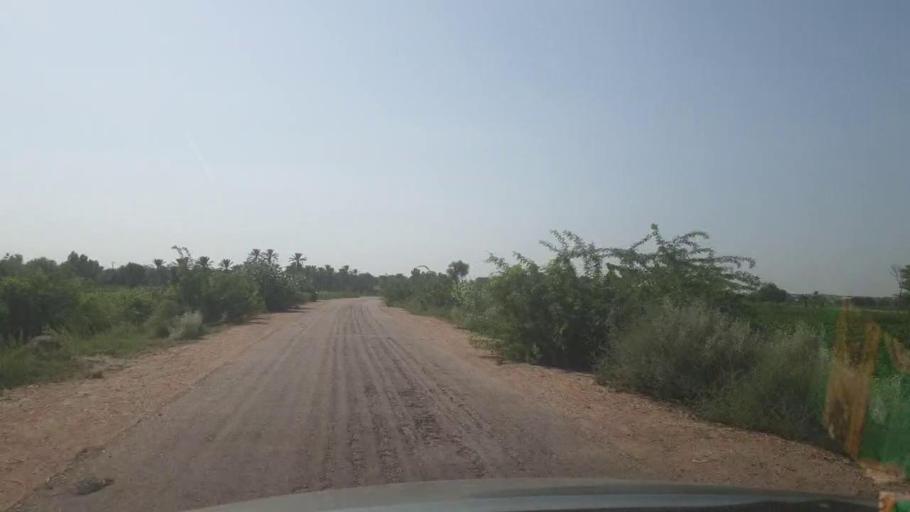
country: PK
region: Sindh
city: Rohri
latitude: 27.4702
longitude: 69.0354
